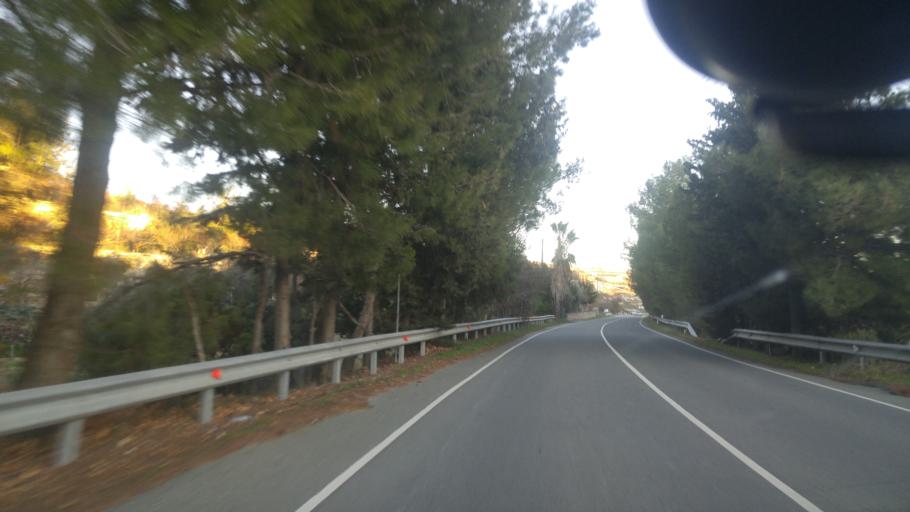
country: CY
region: Limassol
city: Pachna
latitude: 34.7958
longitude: 32.8159
